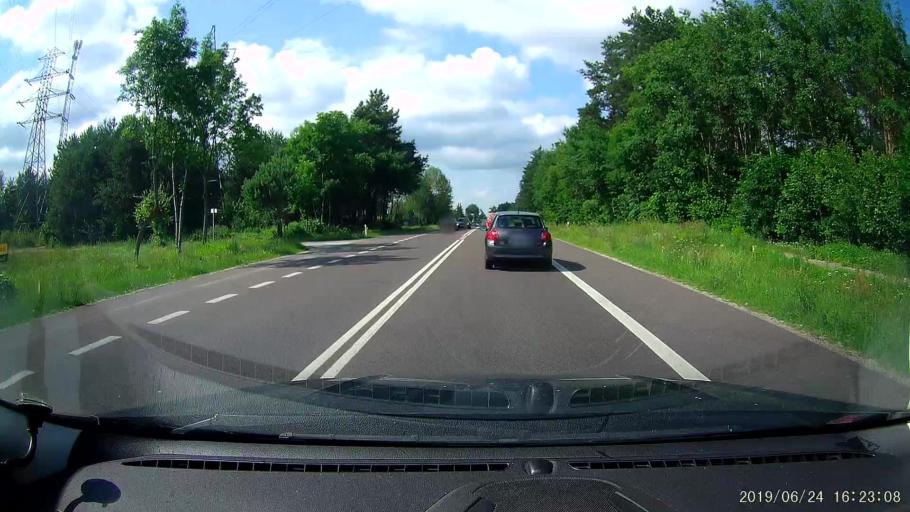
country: PL
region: Lublin Voivodeship
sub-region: Powiat tomaszowski
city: Tomaszow Lubelski
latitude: 50.4286
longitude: 23.4227
